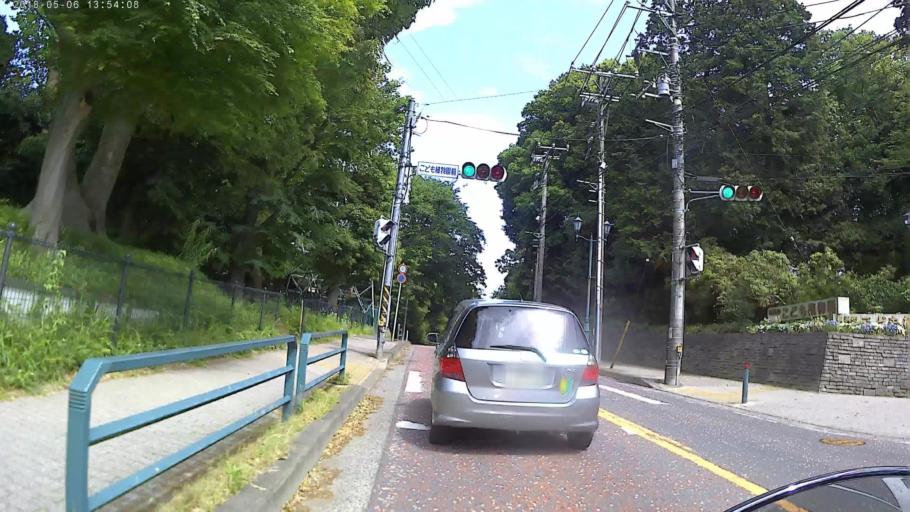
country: JP
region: Kanagawa
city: Yokohama
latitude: 35.4339
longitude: 139.5779
